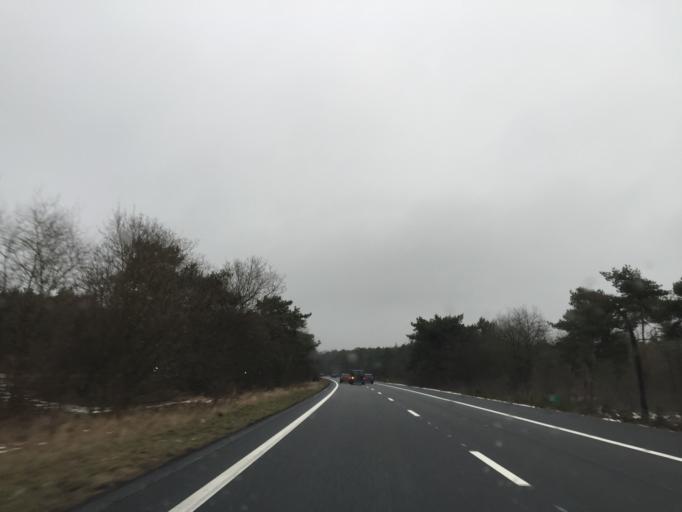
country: NL
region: Gelderland
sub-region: Gemeente Oldebroek
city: Oldebroek
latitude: 52.4409
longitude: 5.9662
